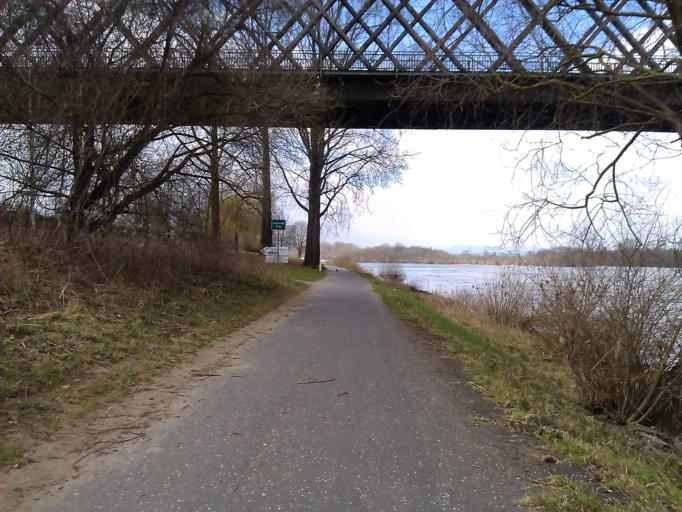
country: DE
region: Rheinland-Pfalz
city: Urmitz
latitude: 50.4198
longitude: 7.5281
